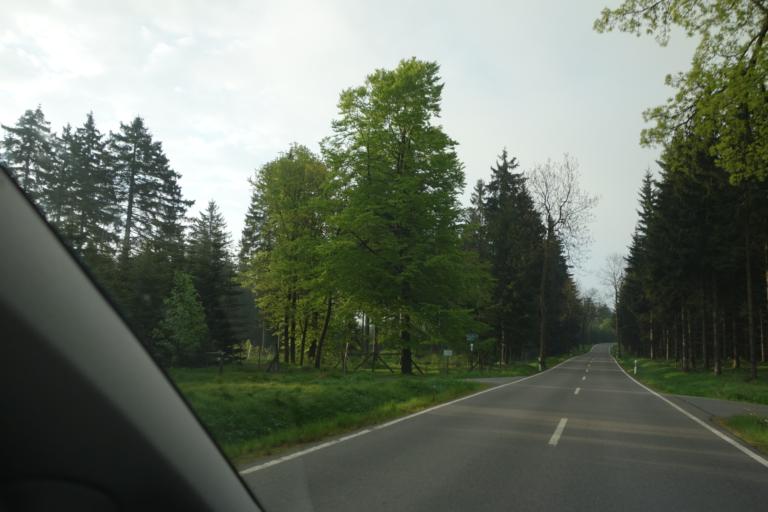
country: DE
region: Saxony
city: Olbernhau
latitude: 50.6105
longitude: 13.2899
